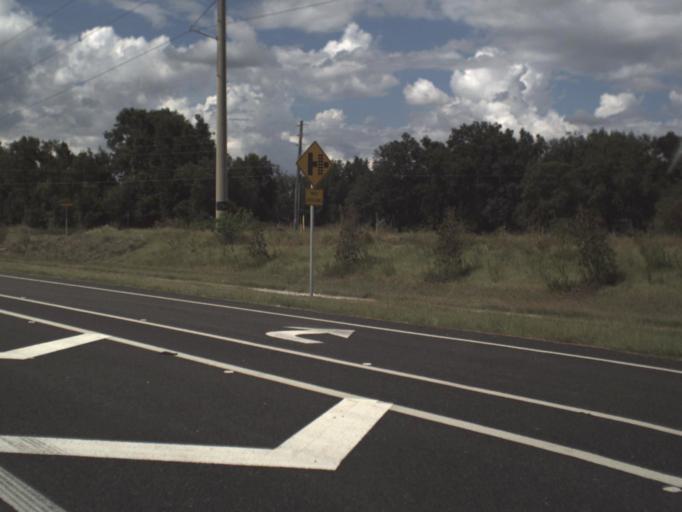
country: US
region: Florida
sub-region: Polk County
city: Highland City
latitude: 27.9521
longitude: -81.8693
